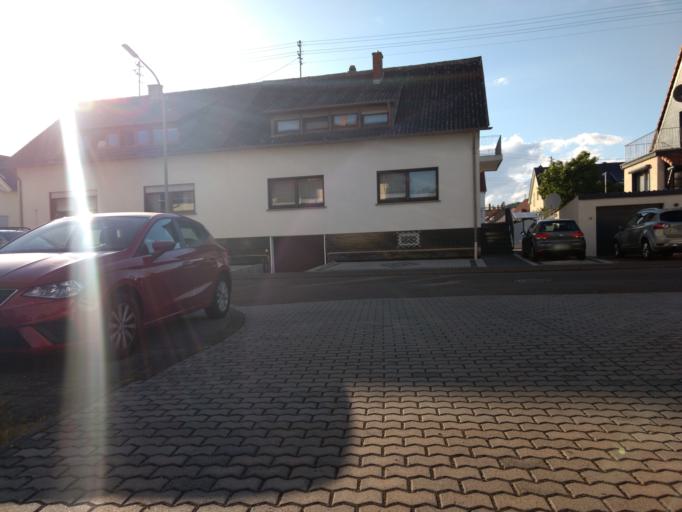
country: DE
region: Saarland
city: Rehlingen-Siersburg
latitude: 49.3779
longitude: 6.6889
